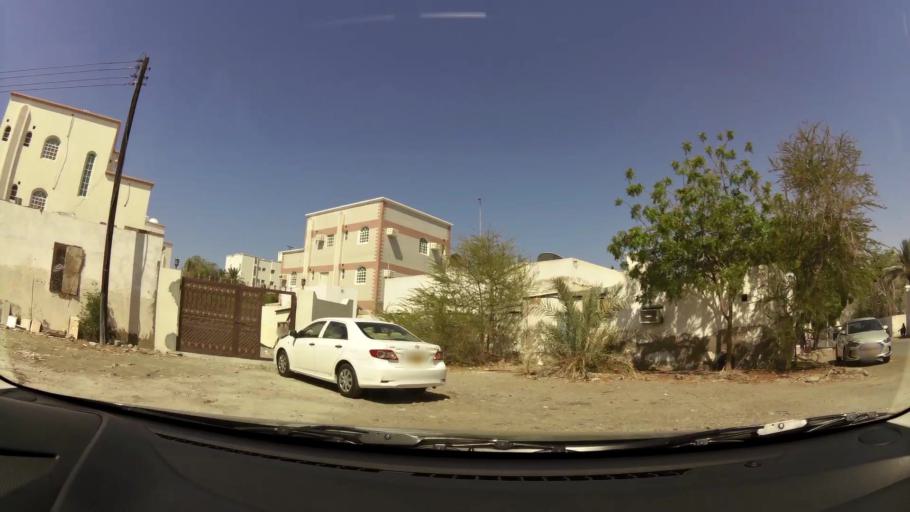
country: OM
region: Muhafazat Masqat
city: As Sib al Jadidah
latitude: 23.6415
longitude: 58.2212
